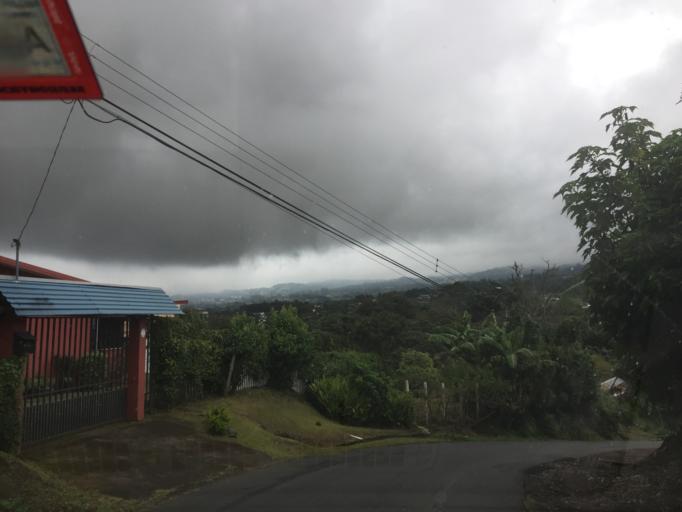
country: CR
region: Heredia
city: Angeles
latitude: 10.0107
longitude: -84.0333
